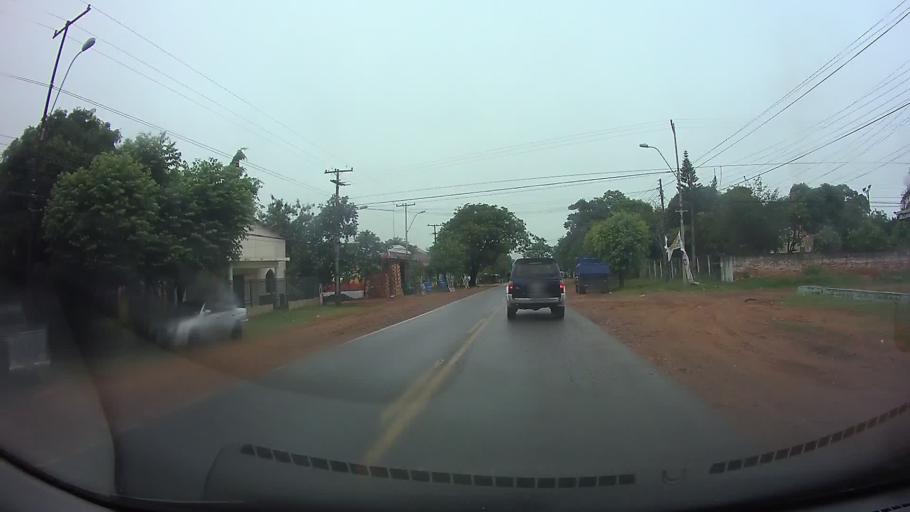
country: PY
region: Central
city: Ita
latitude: -25.5002
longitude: -57.3573
